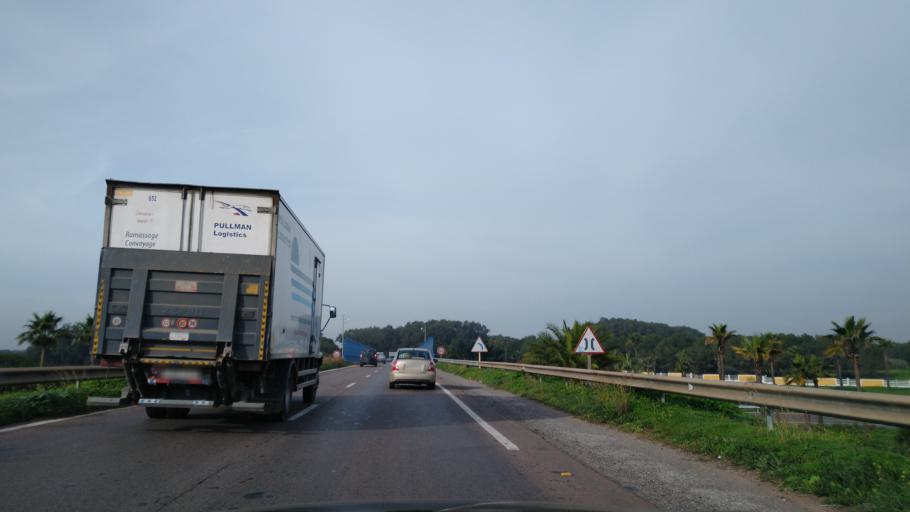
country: MA
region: Rabat-Sale-Zemmour-Zaer
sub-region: Skhirate-Temara
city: Temara
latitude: 33.9499
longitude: -6.9163
